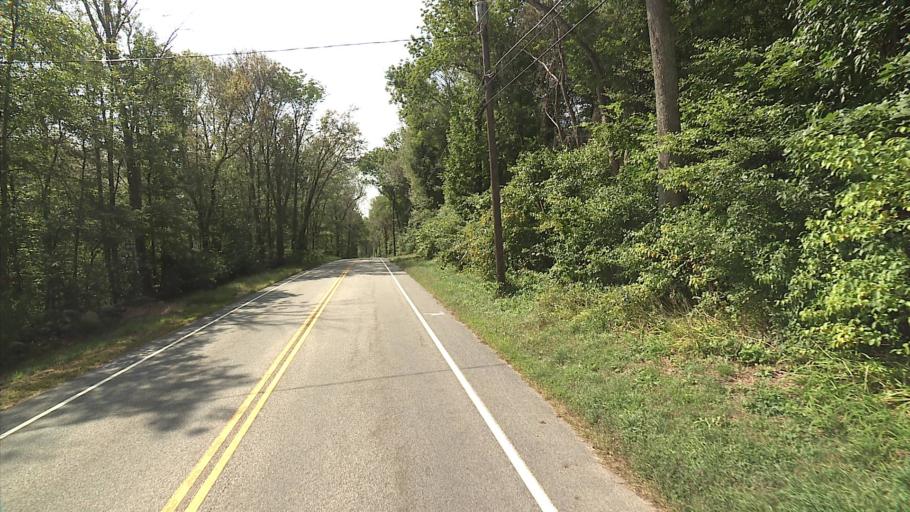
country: US
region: Connecticut
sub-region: Windham County
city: Wauregan
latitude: 41.7227
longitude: -71.9691
